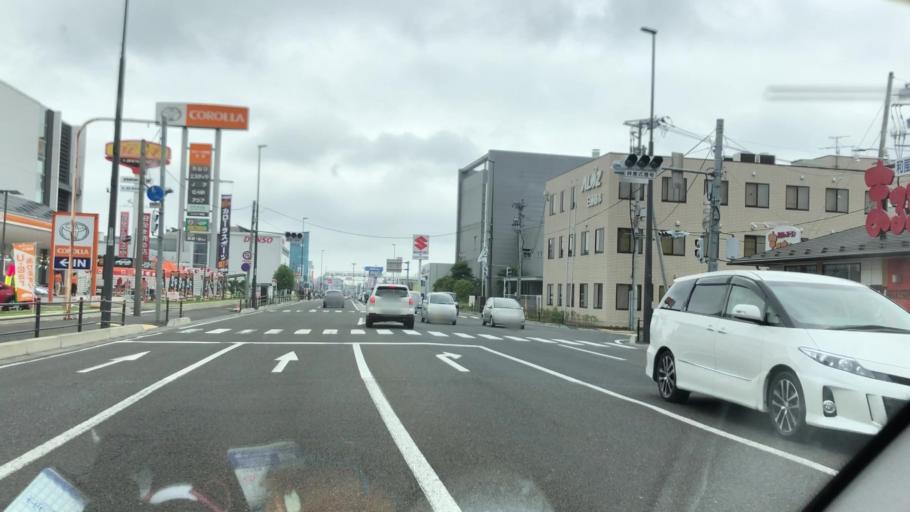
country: JP
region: Miyagi
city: Sendai-shi
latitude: 38.2696
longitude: 140.9250
